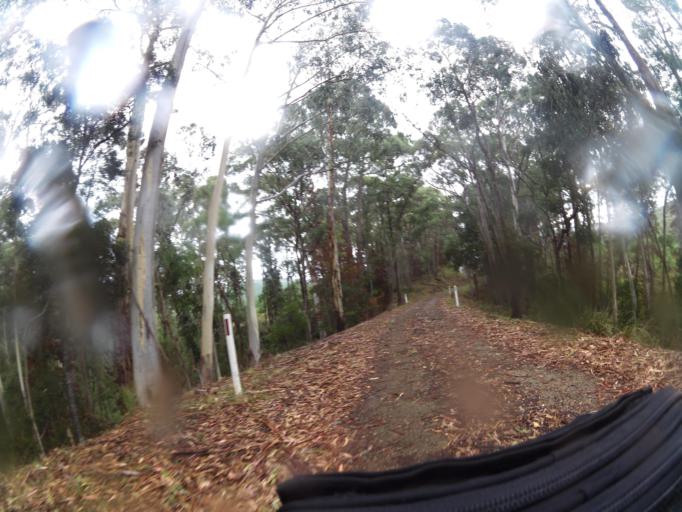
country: AU
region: New South Wales
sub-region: Greater Hume Shire
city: Holbrook
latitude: -36.2245
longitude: 147.5795
